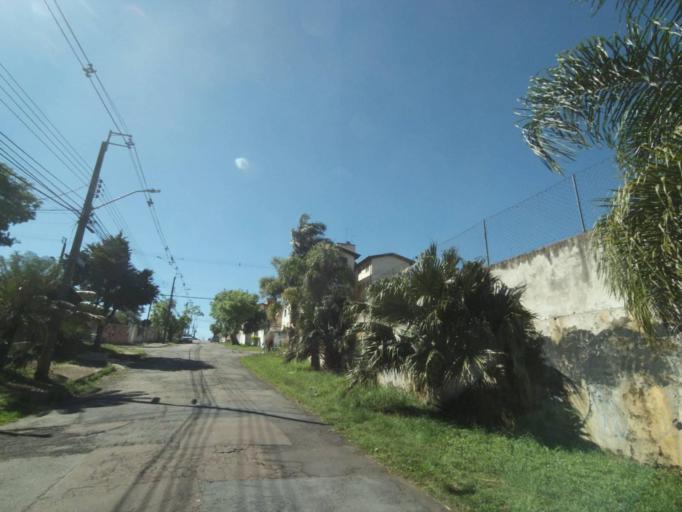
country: BR
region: Parana
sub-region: Curitiba
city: Curitiba
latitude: -25.4568
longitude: -49.3524
